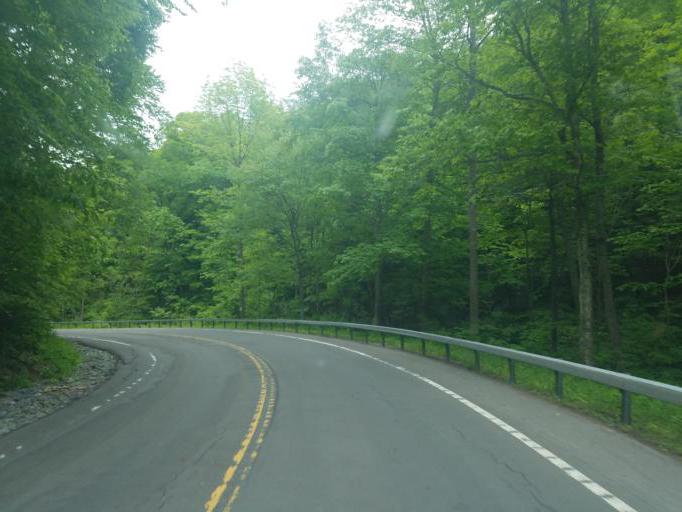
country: US
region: New York
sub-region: Herkimer County
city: Frankfort
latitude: 42.9556
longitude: -75.1132
